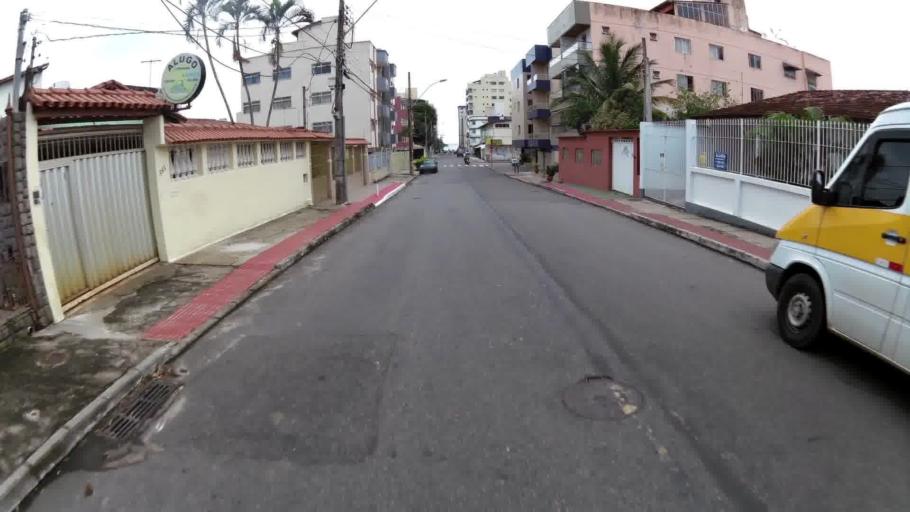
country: BR
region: Espirito Santo
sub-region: Guarapari
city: Guarapari
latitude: -20.6521
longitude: -40.4908
